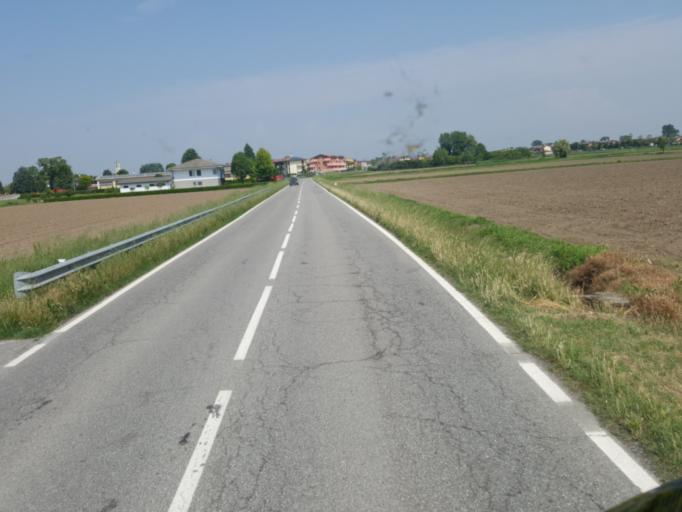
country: IT
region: Lombardy
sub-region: Provincia di Lodi
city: Boffalora d'Adda
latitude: 45.3518
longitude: 9.4962
